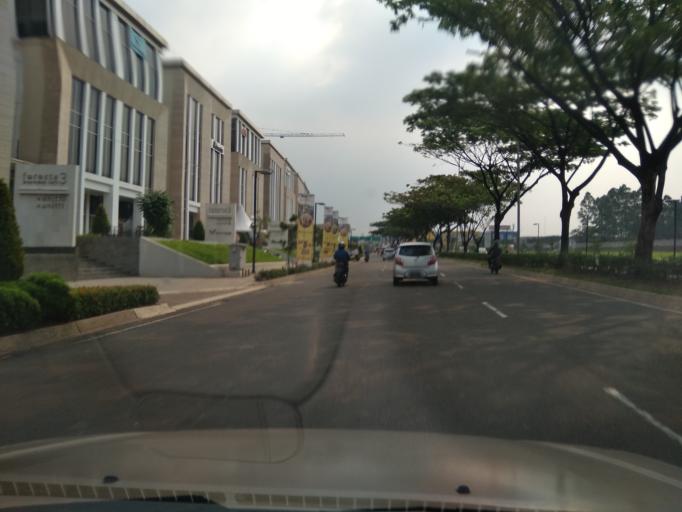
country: ID
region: West Java
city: Serpong
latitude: -6.2874
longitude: 106.6418
